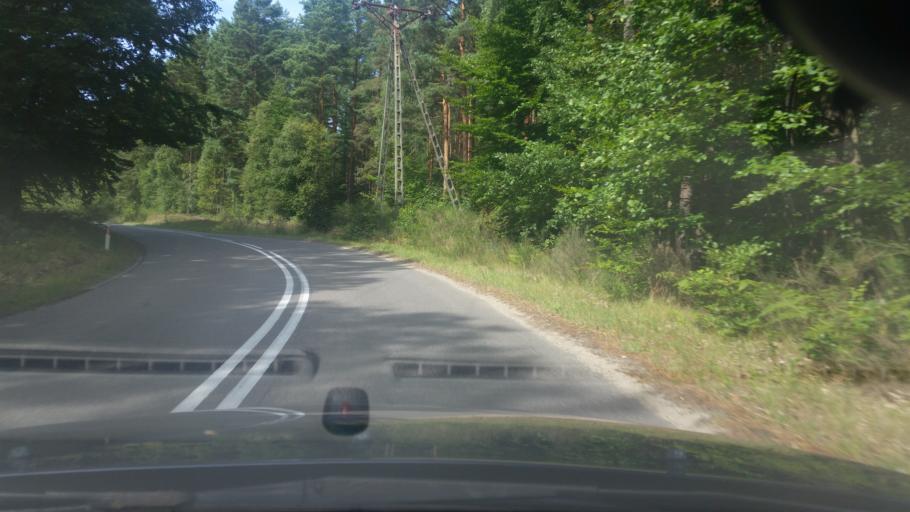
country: PL
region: Pomeranian Voivodeship
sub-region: Powiat wejherowski
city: Choczewo
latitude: 54.7467
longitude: 17.7352
